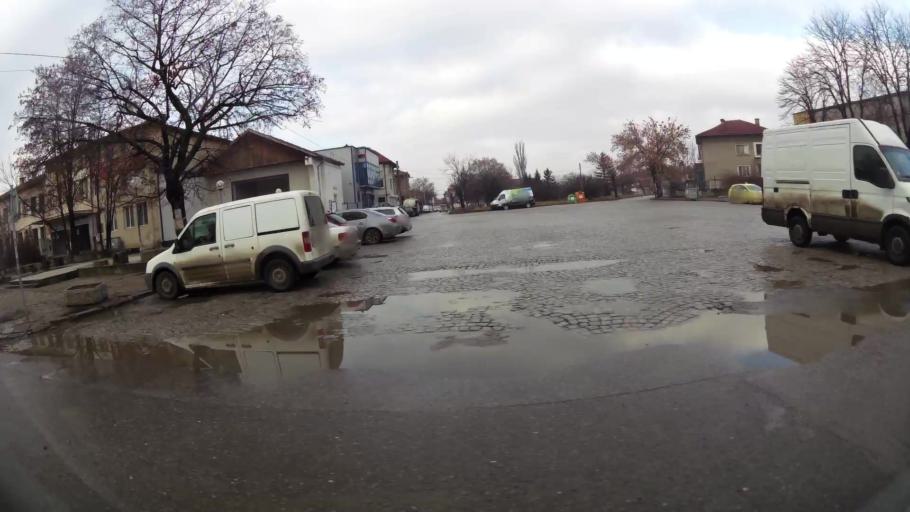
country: BG
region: Sofia-Capital
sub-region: Stolichna Obshtina
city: Sofia
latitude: 42.7380
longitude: 23.3436
